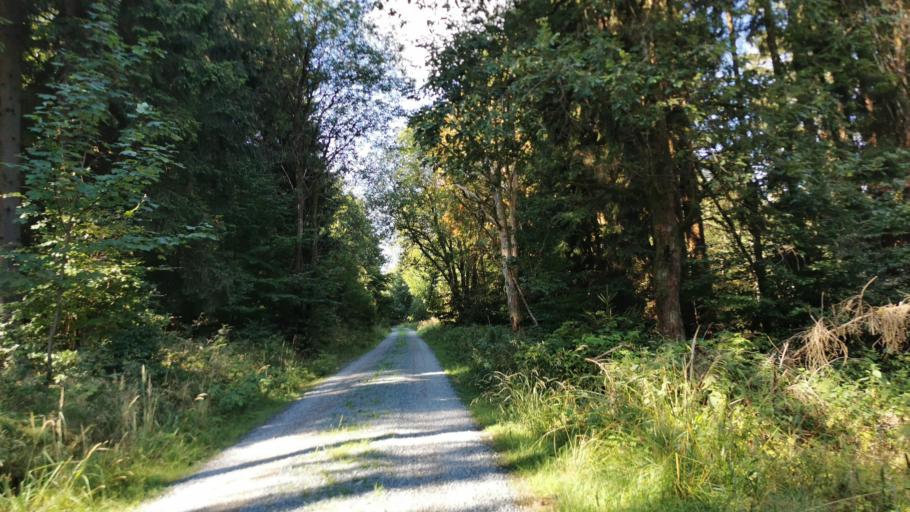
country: DE
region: Thuringia
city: Schlegel
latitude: 50.3966
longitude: 11.5856
